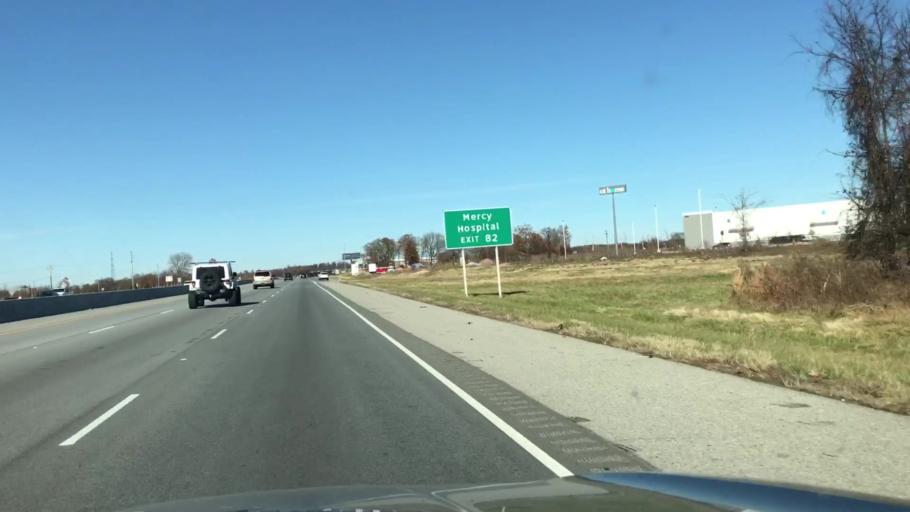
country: US
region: Arkansas
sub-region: Benton County
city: Lowell
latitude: 36.2846
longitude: -94.1572
